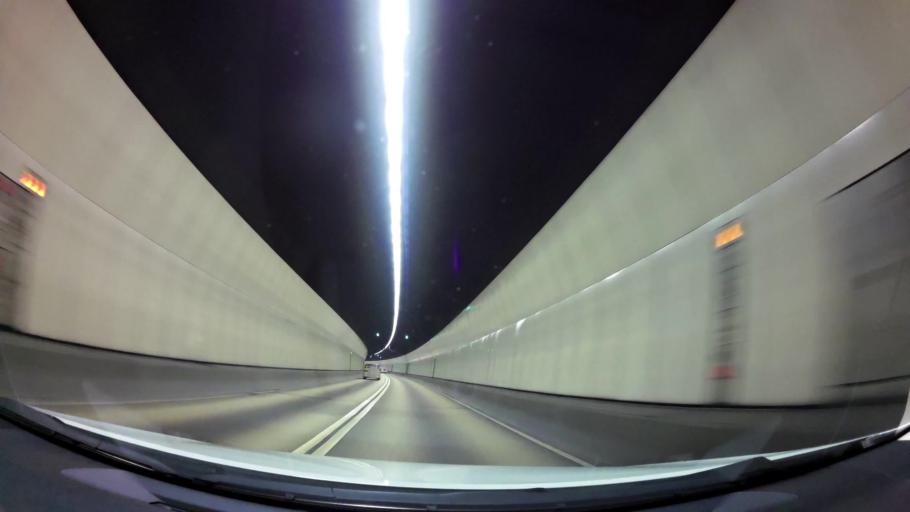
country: HK
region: Sha Tin
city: Sha Tin
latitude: 22.3775
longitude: 114.1461
